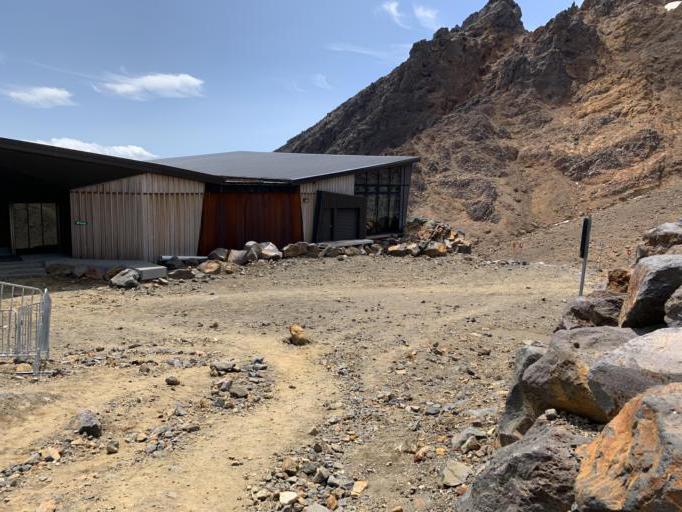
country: NZ
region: Manawatu-Wanganui
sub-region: Ruapehu District
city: Waiouru
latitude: -39.2525
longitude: 175.5644
